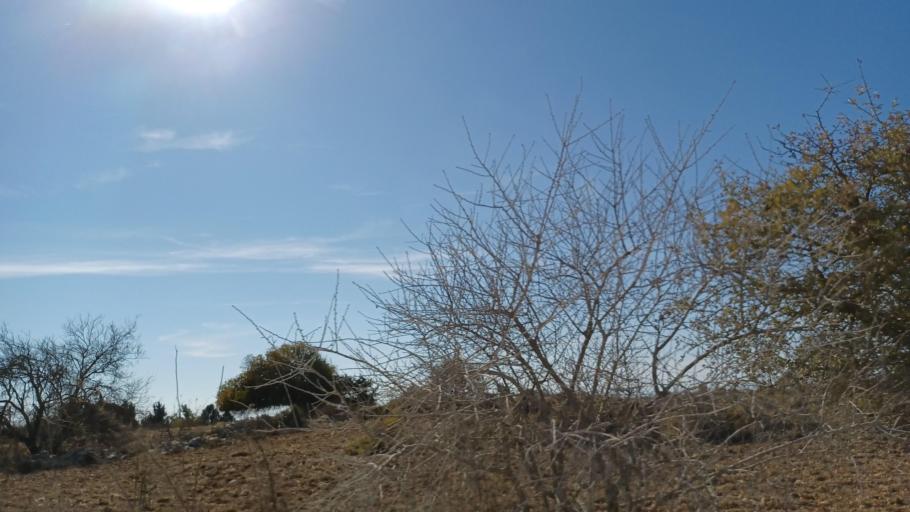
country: CY
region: Pafos
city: Pegeia
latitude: 34.9416
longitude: 32.4074
